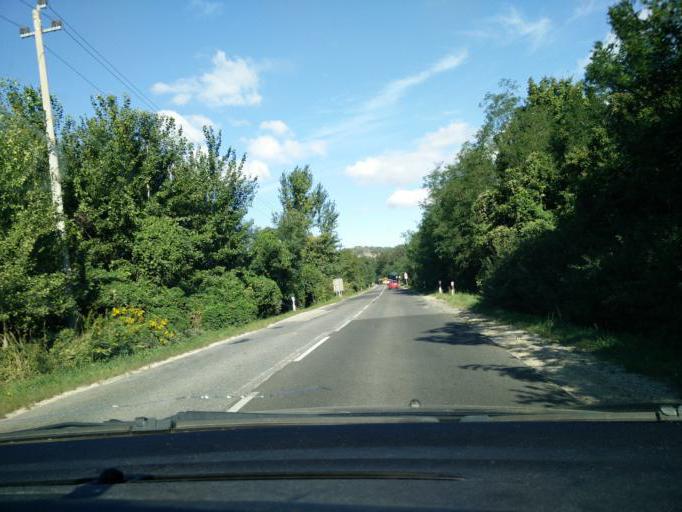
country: HU
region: Pest
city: Piliscsaba
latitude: 47.6482
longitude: 18.8042
